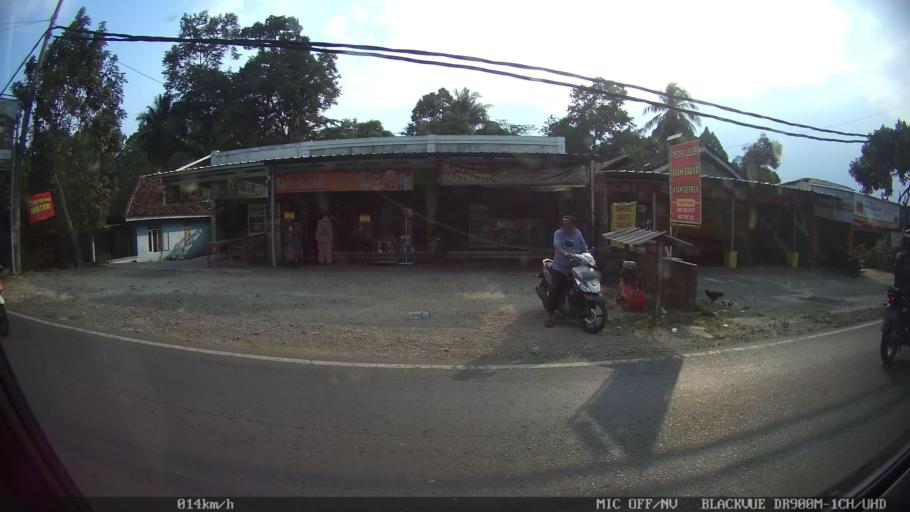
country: ID
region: Lampung
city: Natar
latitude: -5.3691
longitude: 105.1912
